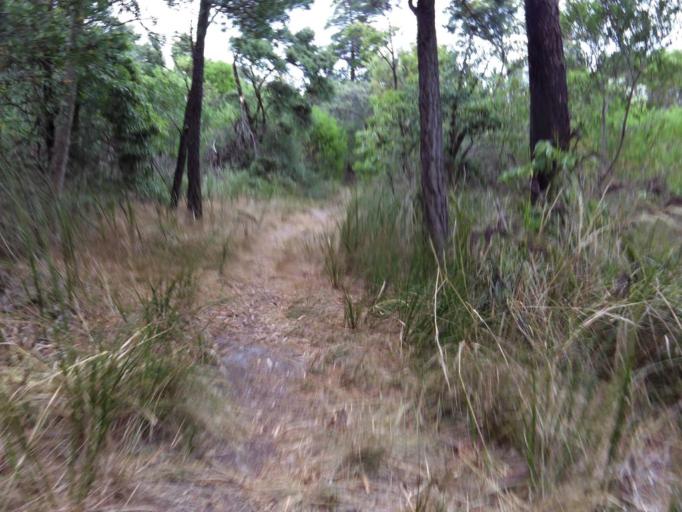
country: AU
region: Victoria
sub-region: Frankston
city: Frankston South
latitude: -38.1733
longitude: 145.1337
